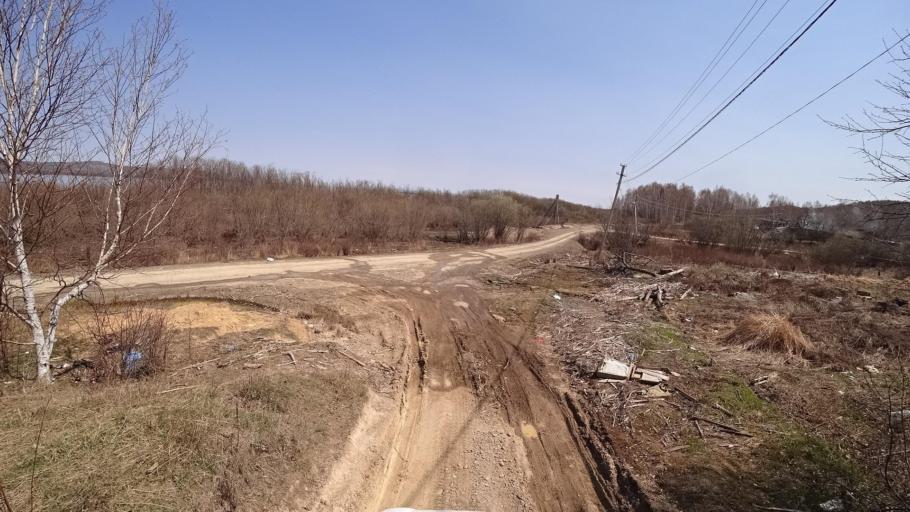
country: RU
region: Khabarovsk Krai
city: Selikhino
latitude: 50.6678
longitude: 137.4037
